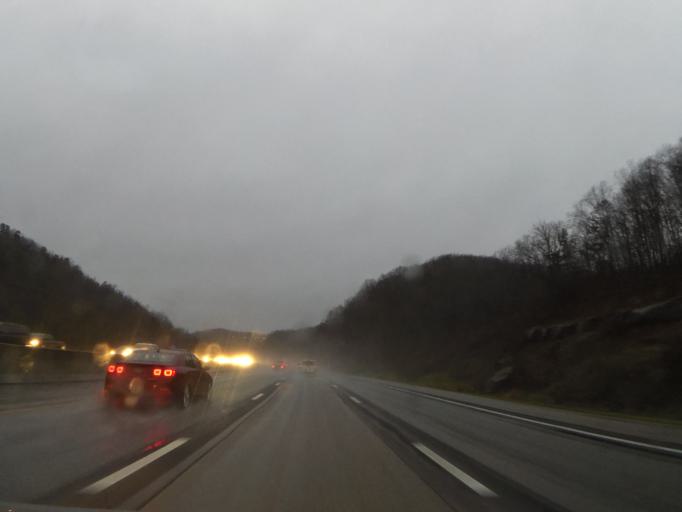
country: US
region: Kentucky
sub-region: Rockcastle County
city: Mount Vernon
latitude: 37.2574
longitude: -84.2491
